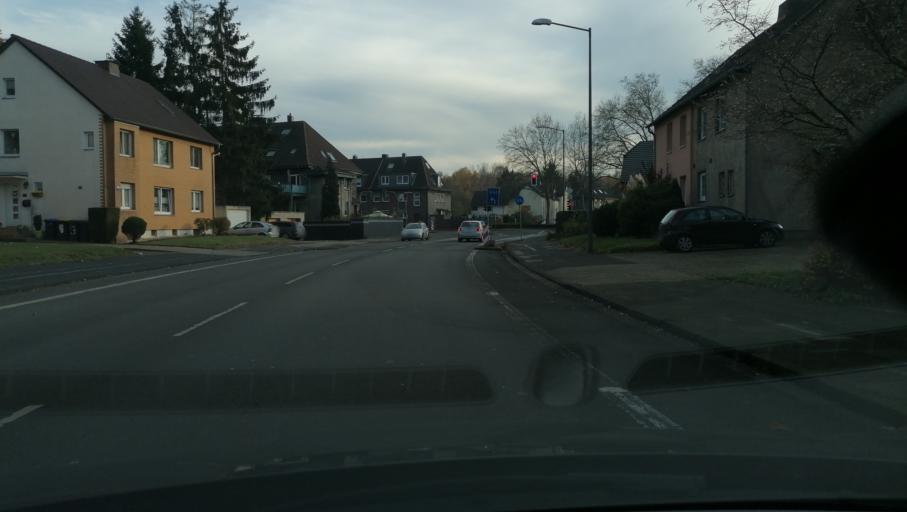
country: DE
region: North Rhine-Westphalia
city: Castrop-Rauxel
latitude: 51.5872
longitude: 7.3214
